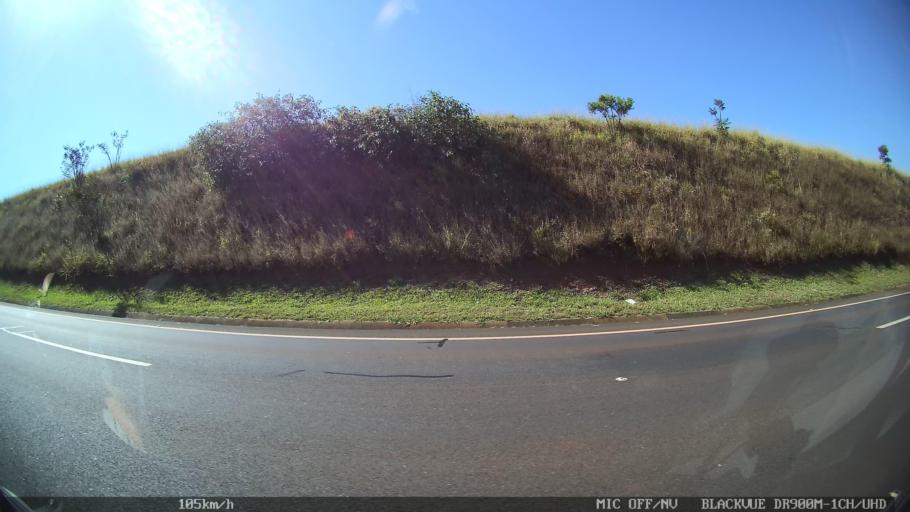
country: BR
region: Sao Paulo
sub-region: Batatais
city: Batatais
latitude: -20.8415
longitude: -47.6015
